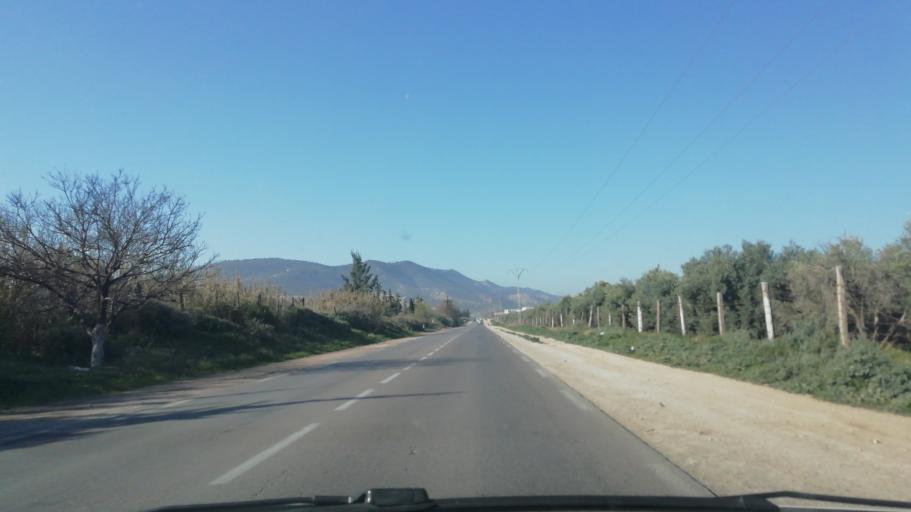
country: DZ
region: Mascara
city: Sig
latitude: 35.5380
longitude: -0.1354
